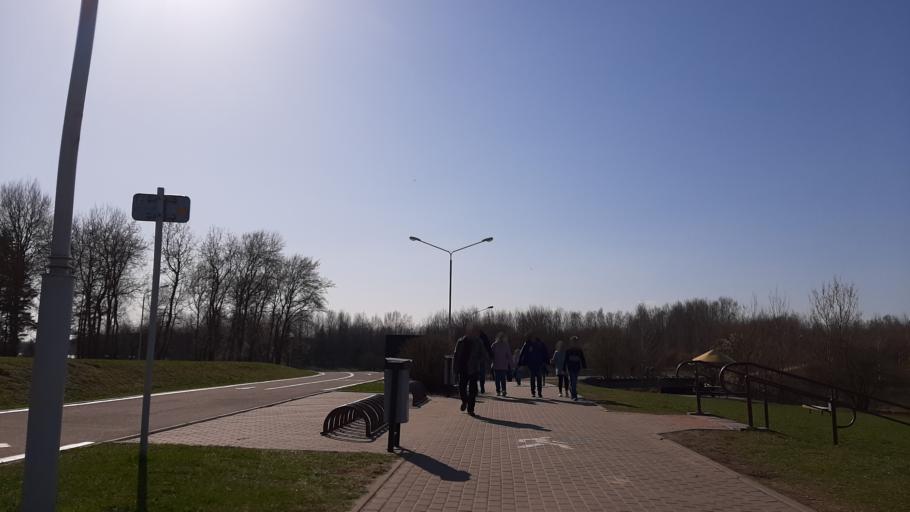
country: BY
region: Minsk
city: Bal'shavik
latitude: 53.9596
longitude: 27.5893
